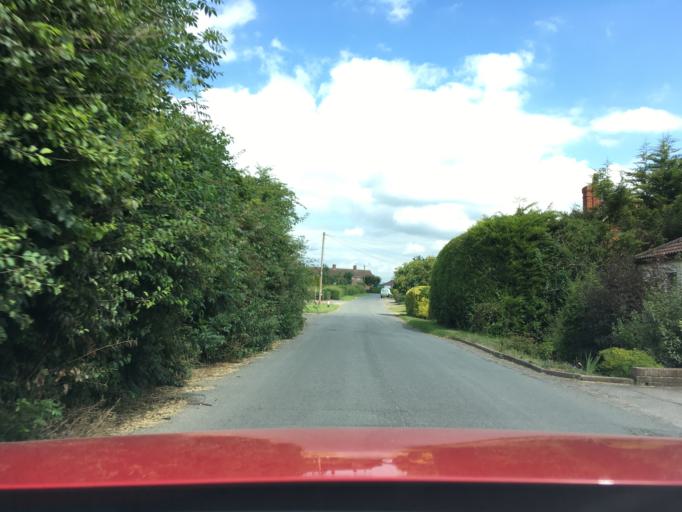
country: GB
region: England
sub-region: Gloucestershire
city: Gloucester
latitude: 51.9057
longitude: -2.2469
